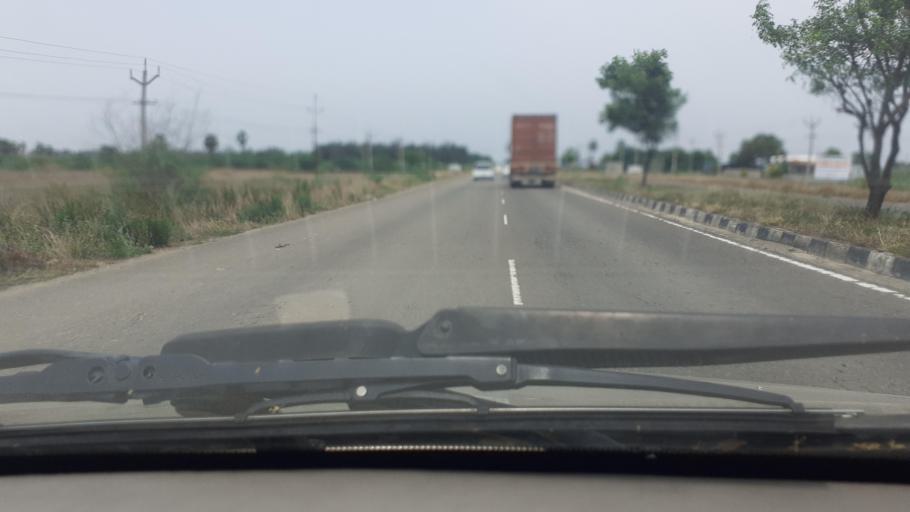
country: IN
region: Tamil Nadu
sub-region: Thoothukkudi
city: Korampallam
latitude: 8.7346
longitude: 77.9812
